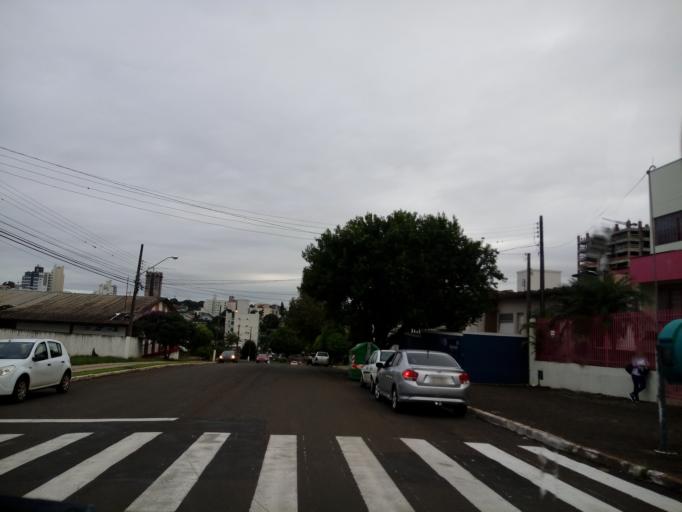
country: BR
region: Santa Catarina
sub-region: Chapeco
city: Chapeco
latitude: -27.0996
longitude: -52.6061
